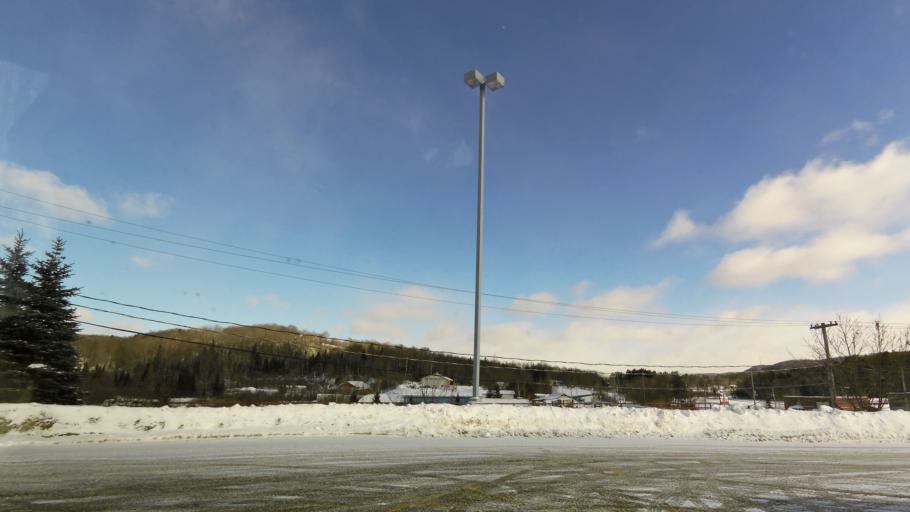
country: CA
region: Ontario
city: Bancroft
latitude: 45.0467
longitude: -78.5349
